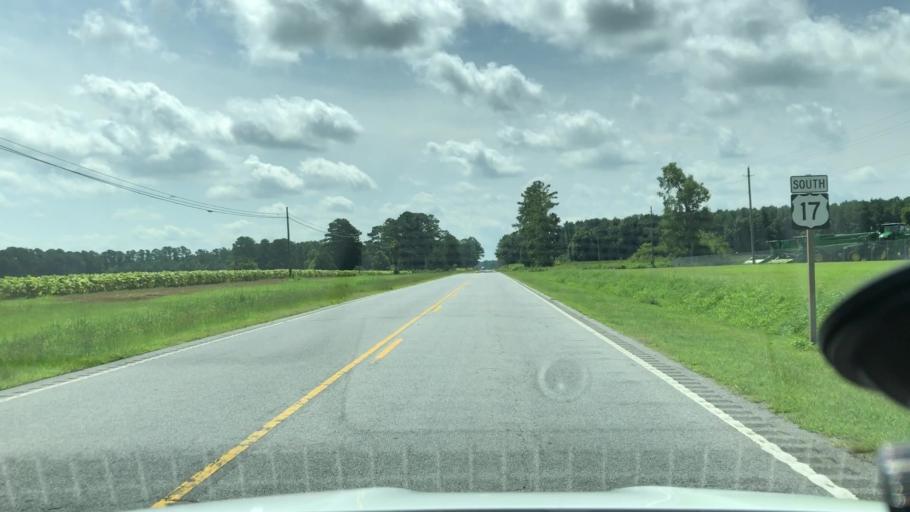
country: US
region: North Carolina
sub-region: Beaufort County
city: Washington
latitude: 35.6511
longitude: -77.0702
